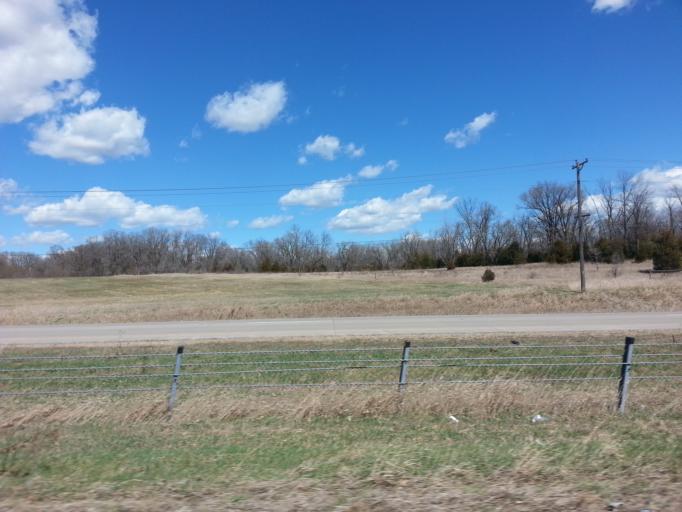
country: US
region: Minnesota
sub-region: Dakota County
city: Hastings
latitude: 44.7846
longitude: -92.8761
